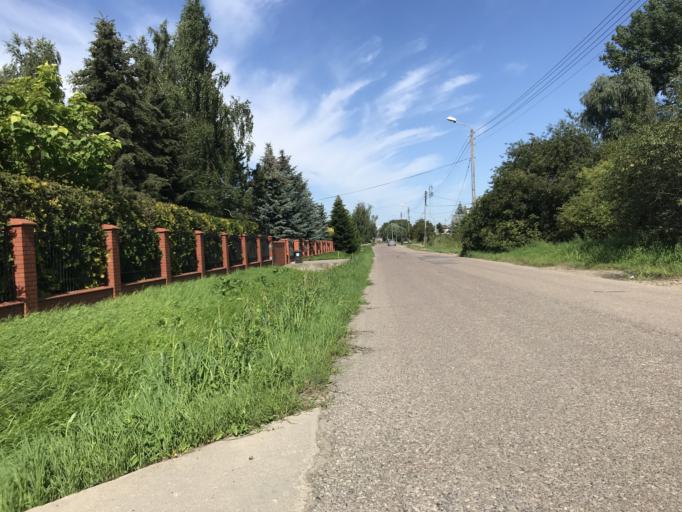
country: PL
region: Pomeranian Voivodeship
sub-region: Gdansk
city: Gdansk
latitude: 54.3318
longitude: 18.6811
